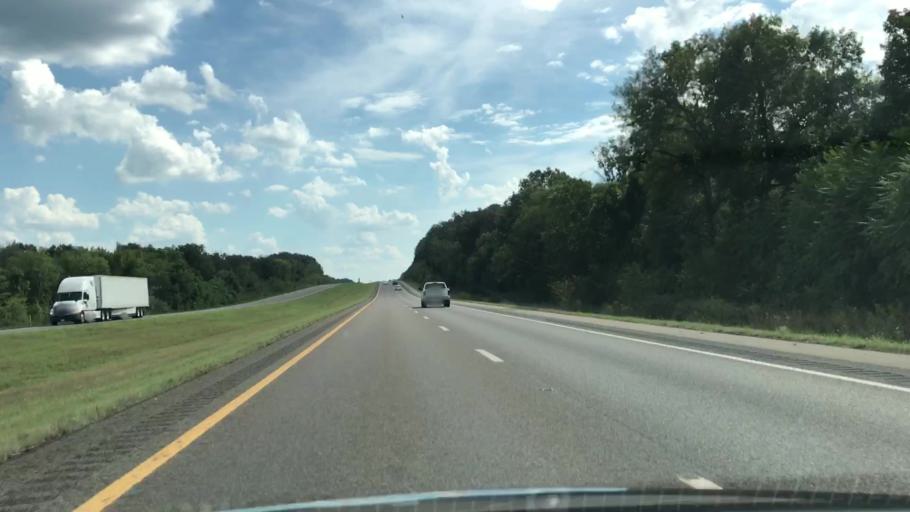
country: US
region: Tennessee
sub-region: Maury County
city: Columbia
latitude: 35.6157
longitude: -86.9003
